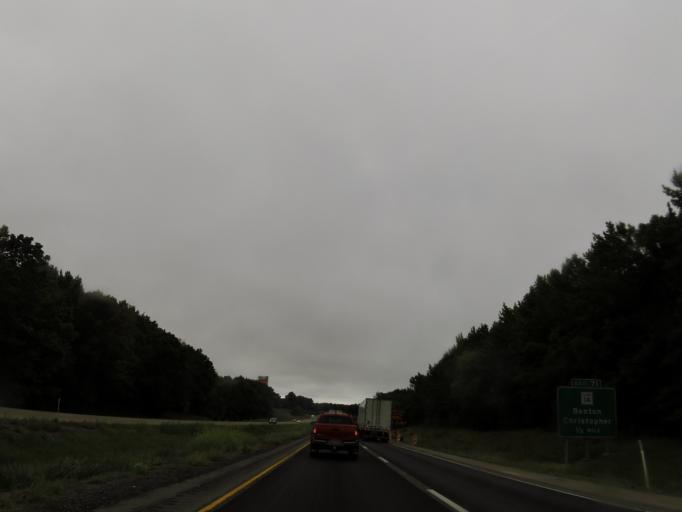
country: US
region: Illinois
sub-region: Franklin County
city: Benton
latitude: 37.9864
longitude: -88.9353
